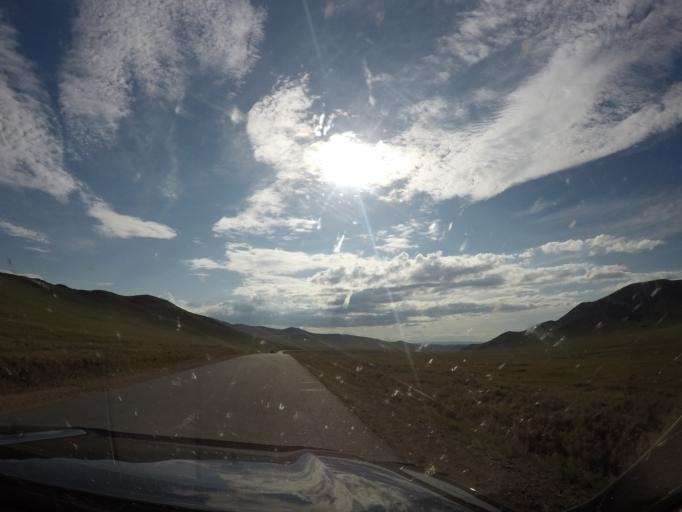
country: MN
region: Central Aimak
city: Bayandelger
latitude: 47.6964
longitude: 108.5470
